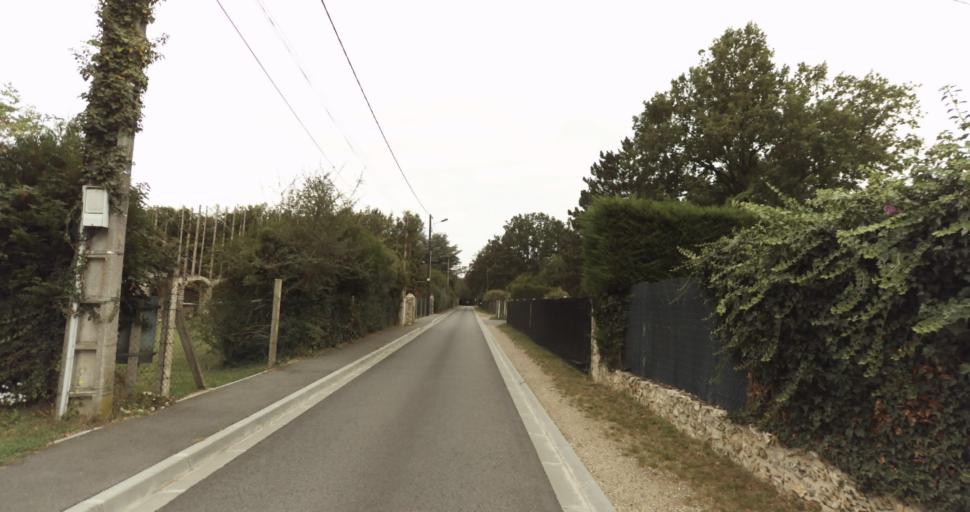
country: FR
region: Haute-Normandie
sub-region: Departement de l'Eure
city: Marcilly-sur-Eure
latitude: 48.8338
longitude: 1.3116
